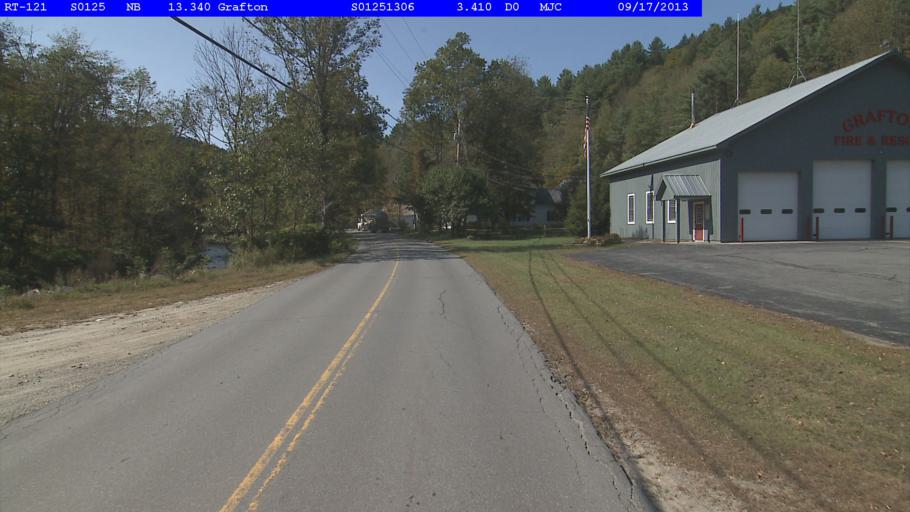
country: US
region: Vermont
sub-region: Windsor County
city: Chester
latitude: 43.1741
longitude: -72.5958
